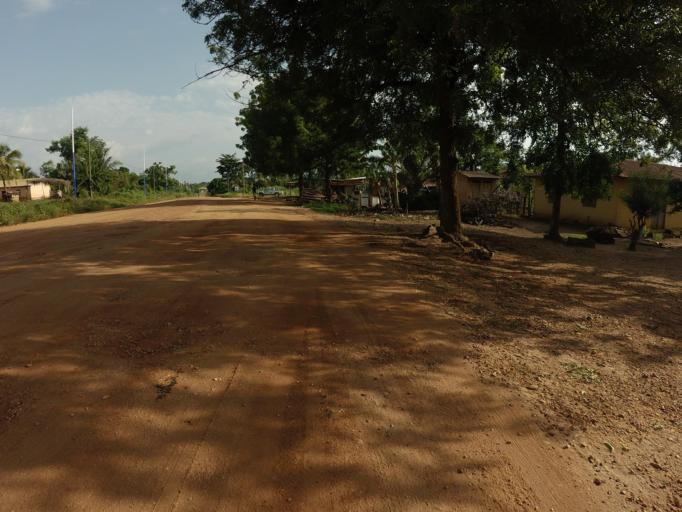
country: GH
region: Volta
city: Hohoe
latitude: 7.1224
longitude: 0.4586
